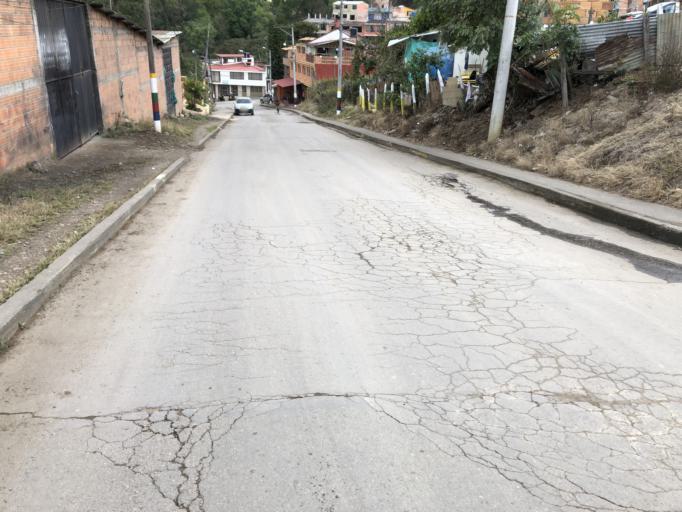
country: CO
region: Cundinamarca
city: Gacheta
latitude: 4.8173
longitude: -73.6393
